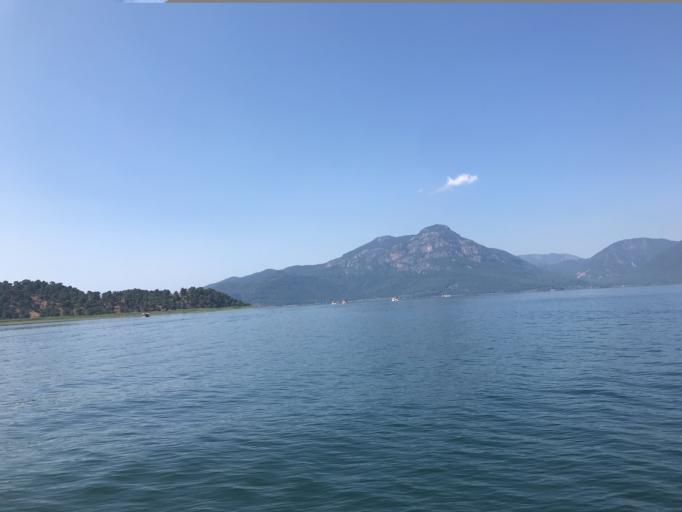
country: TR
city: Dalyan
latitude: 36.9060
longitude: 28.6494
